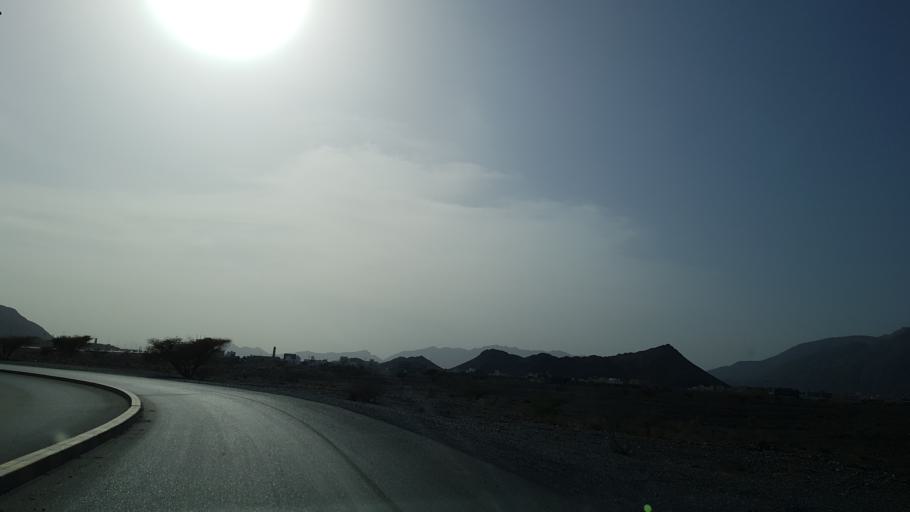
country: OM
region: Muhafazat ad Dakhiliyah
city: Izki
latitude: 22.8924
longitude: 57.6841
